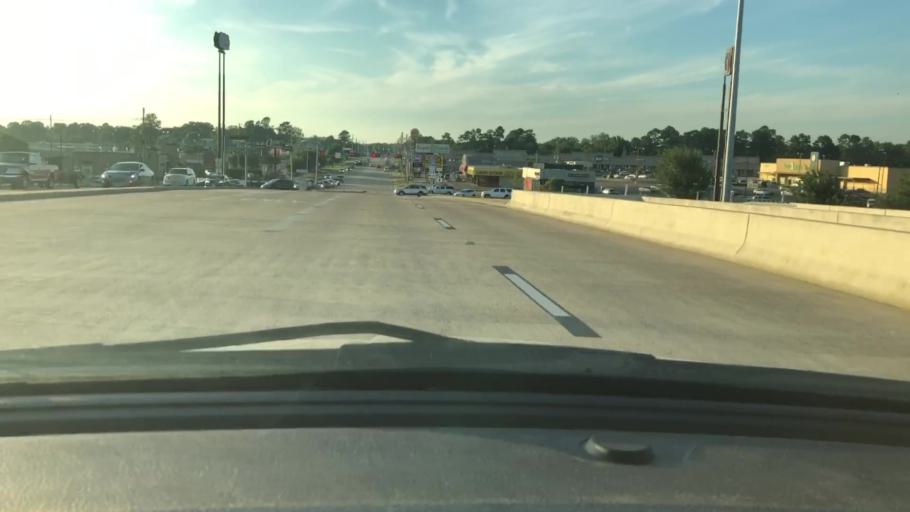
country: US
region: Texas
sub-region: Bowie County
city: Wake Village
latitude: 33.4566
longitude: -94.0869
